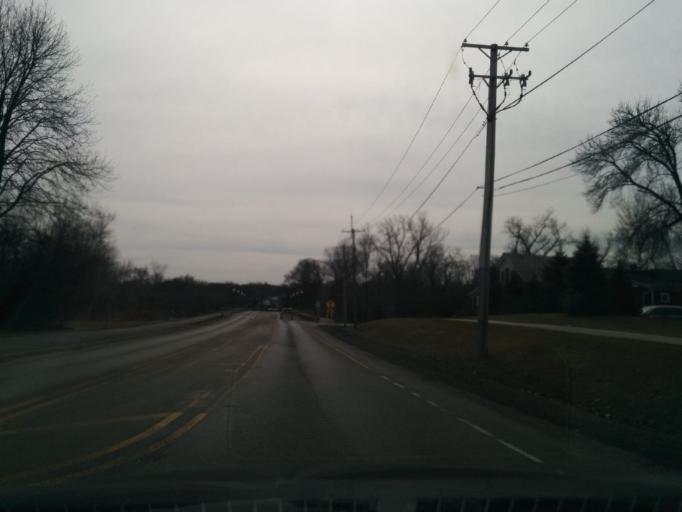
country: US
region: Illinois
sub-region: DuPage County
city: Oak Brook
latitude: 41.8221
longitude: -87.9266
